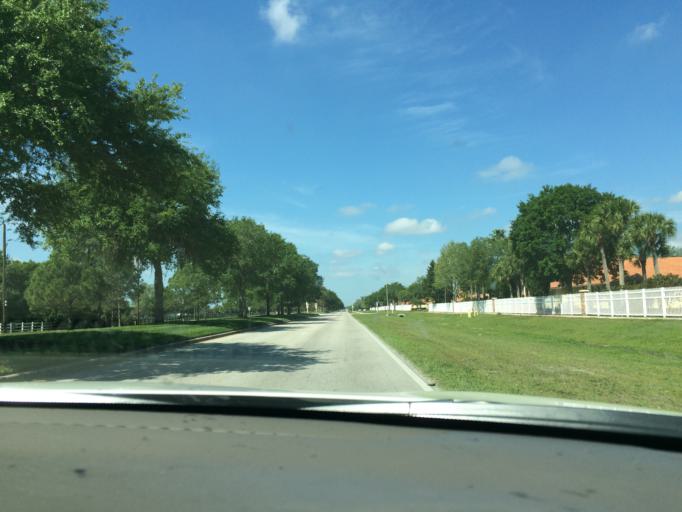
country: US
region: Florida
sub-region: Sarasota County
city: The Meadows
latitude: 27.3866
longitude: -82.4047
